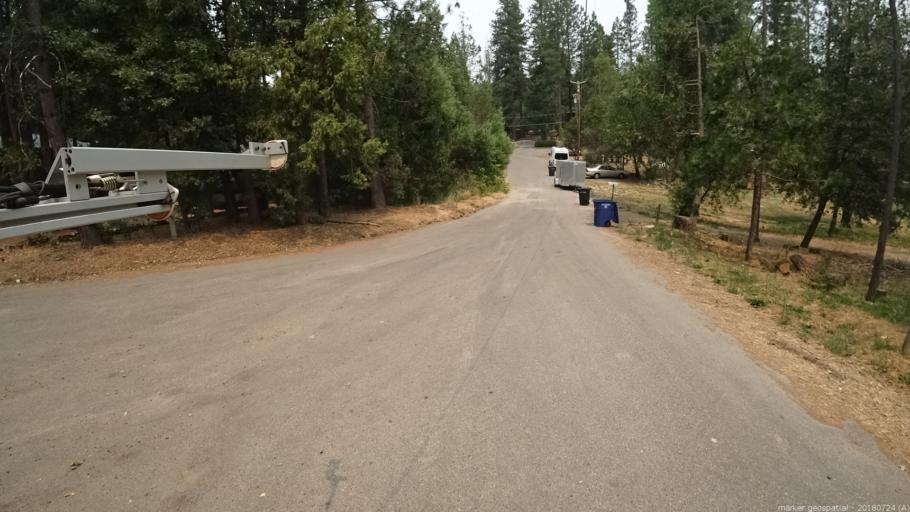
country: US
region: California
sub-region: Madera County
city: Oakhurst
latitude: 37.3205
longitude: -119.5833
